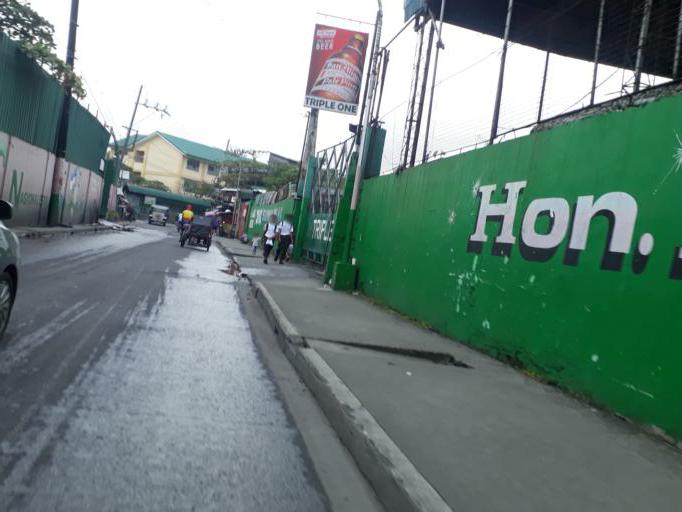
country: PH
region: Metro Manila
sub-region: Caloocan City
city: Niugan
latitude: 14.6593
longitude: 120.9670
